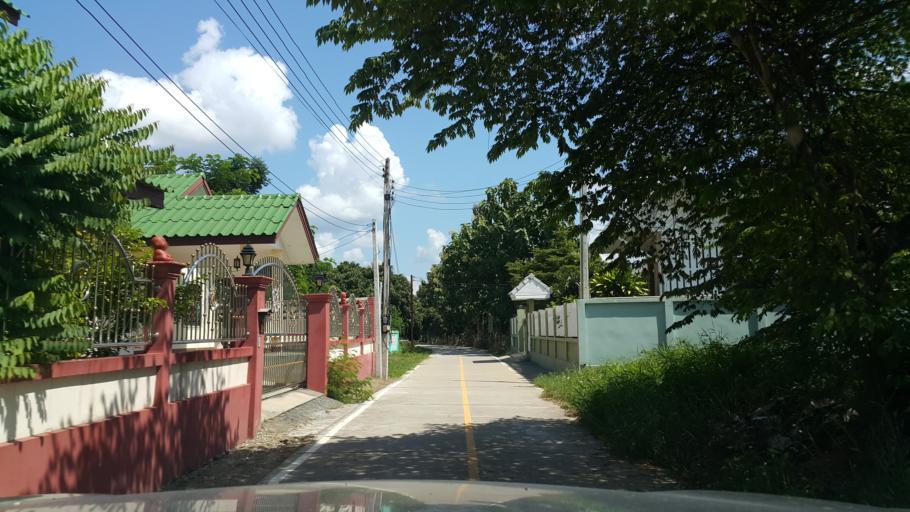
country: TH
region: Chiang Mai
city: Chom Thong
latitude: 18.4206
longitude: 98.6826
